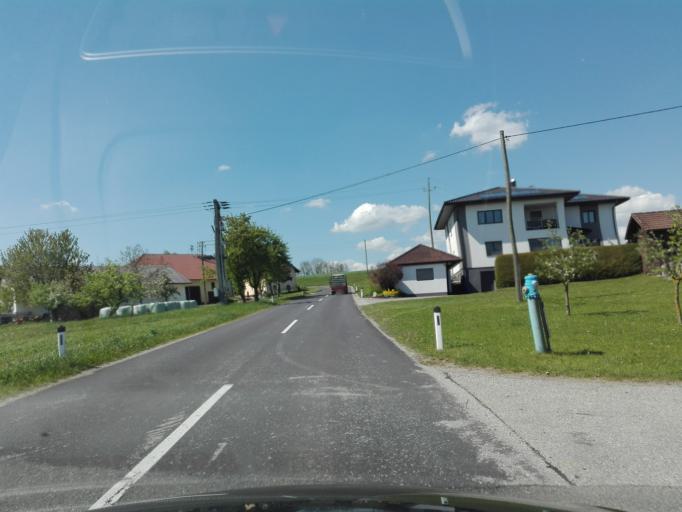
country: AT
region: Upper Austria
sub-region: Politischer Bezirk Urfahr-Umgebung
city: Feldkirchen an der Donau
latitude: 48.3503
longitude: 13.9445
